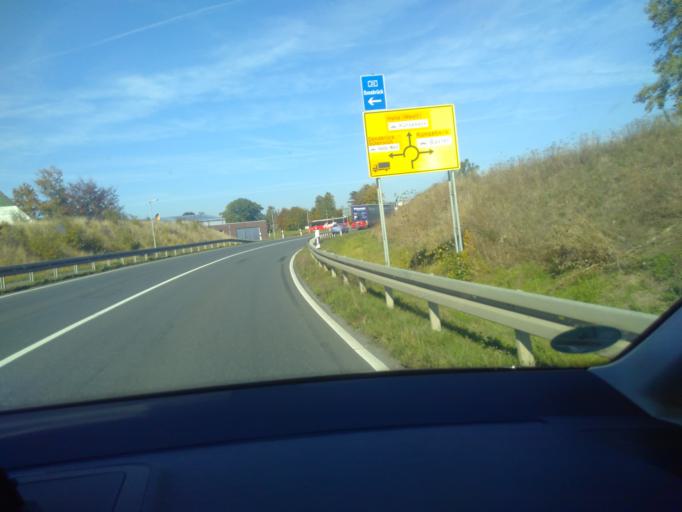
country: DE
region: North Rhine-Westphalia
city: Halle
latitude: 52.0328
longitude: 8.3746
